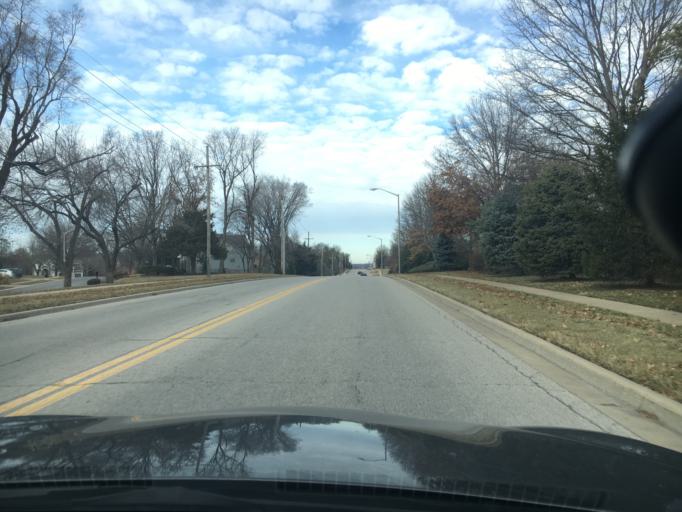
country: US
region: Kansas
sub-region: Johnson County
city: Leawood
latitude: 38.8954
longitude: -94.6305
